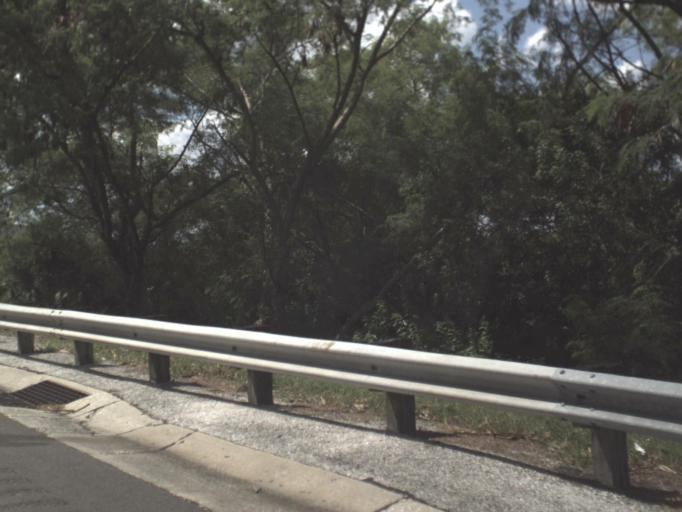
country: US
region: Florida
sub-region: Hillsborough County
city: Palm River-Clair Mel
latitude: 27.9501
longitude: -82.3937
